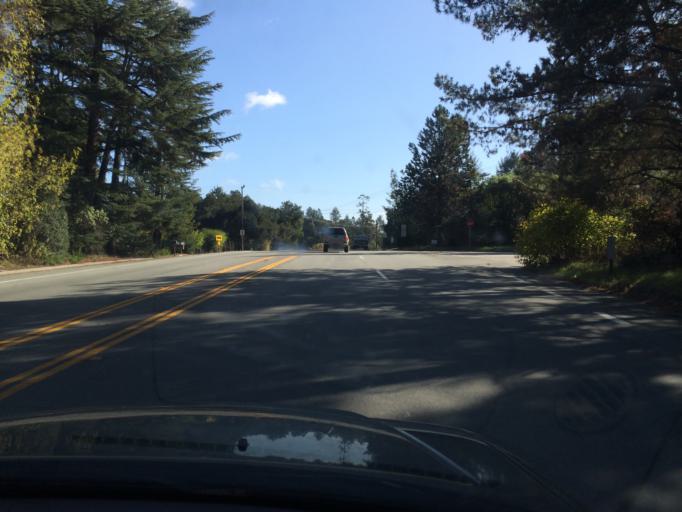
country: US
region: California
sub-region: Santa Cruz County
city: Mount Hermon
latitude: 37.0542
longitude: -122.0402
